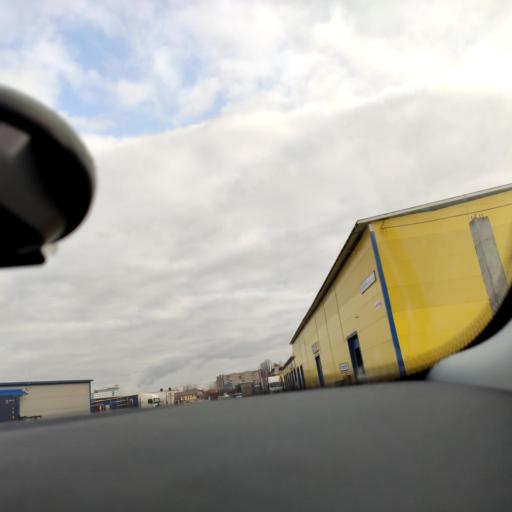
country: RU
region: Moskovskaya
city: Mosrentgen
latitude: 55.6233
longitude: 37.4623
